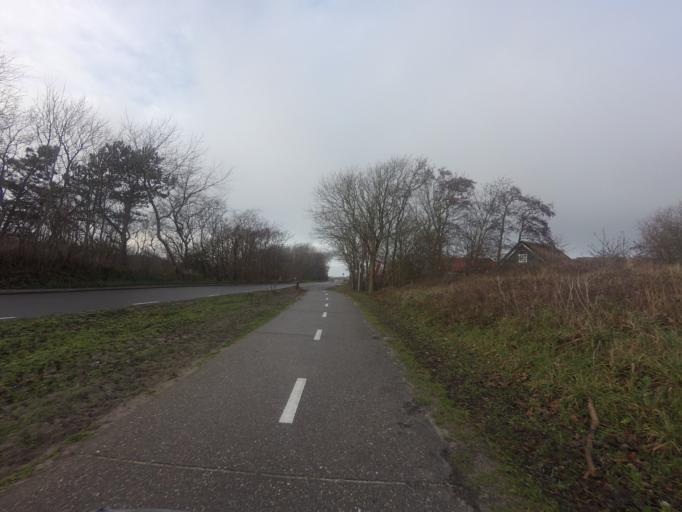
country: NL
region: North Holland
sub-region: Gemeente Texel
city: Den Burg
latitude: 53.1573
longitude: 4.8443
